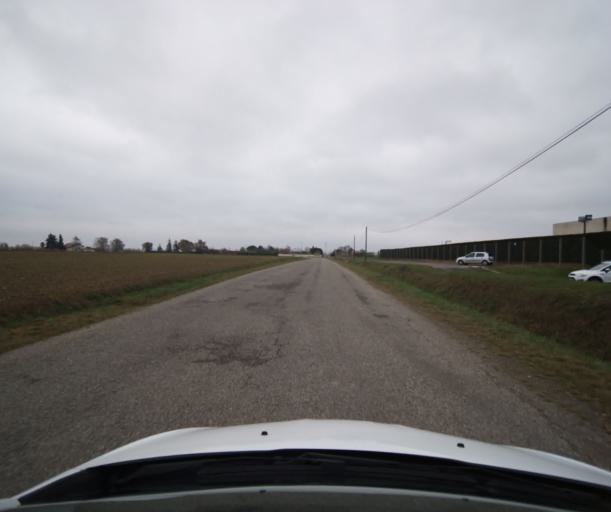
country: FR
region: Midi-Pyrenees
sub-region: Departement du Tarn-et-Garonne
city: Castelsarrasin
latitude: 44.0684
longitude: 1.1123
